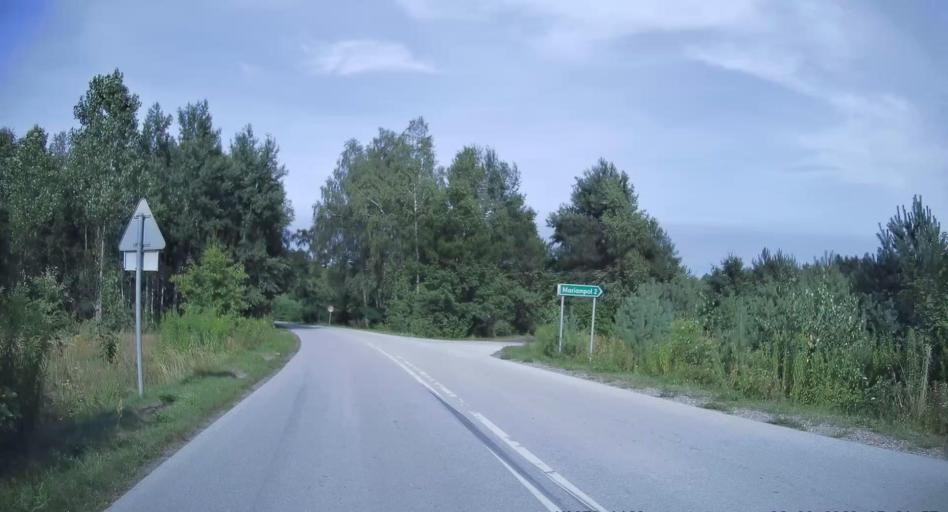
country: PL
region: Lodz Voivodeship
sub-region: Powiat opoczynski
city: Mniszkow
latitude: 51.3373
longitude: 20.0370
